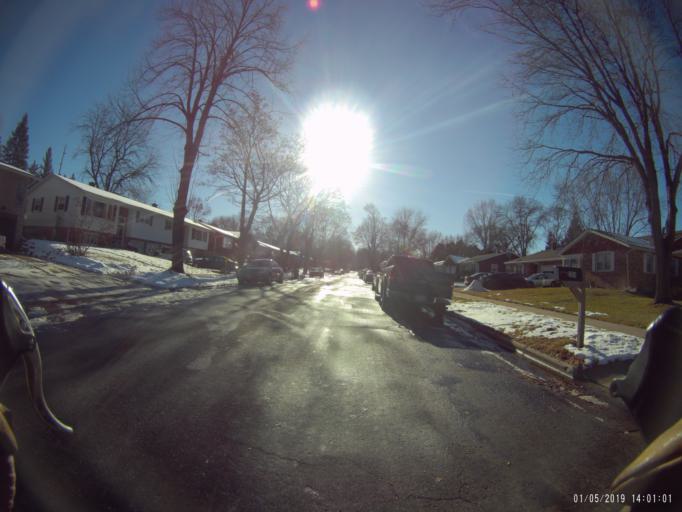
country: US
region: Wisconsin
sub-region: Dane County
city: Madison
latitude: 43.0291
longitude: -89.4230
